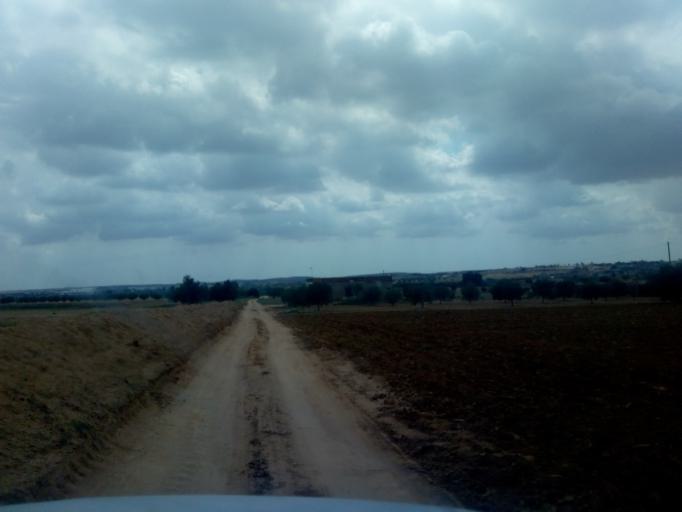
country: TN
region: Safaqis
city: Sfax
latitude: 34.7449
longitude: 10.4906
